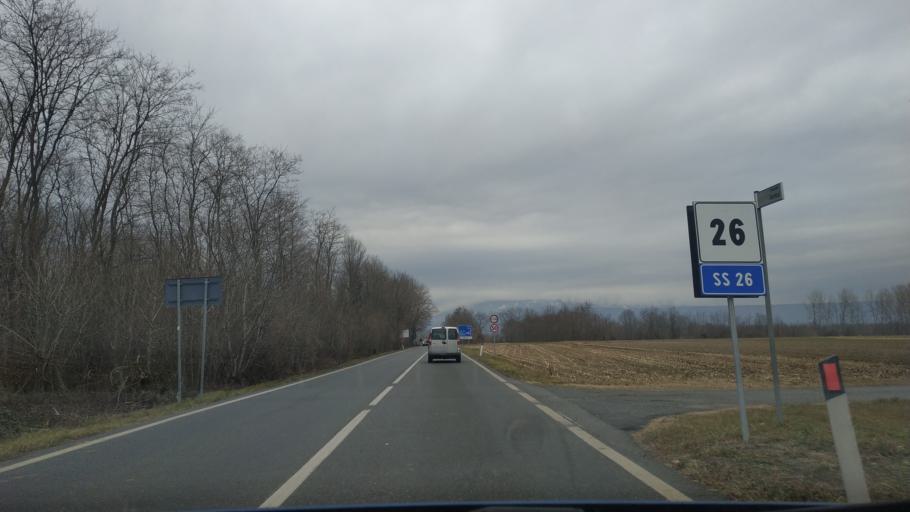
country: IT
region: Piedmont
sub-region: Provincia di Torino
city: Romano Canavese
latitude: 45.4086
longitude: 7.8822
